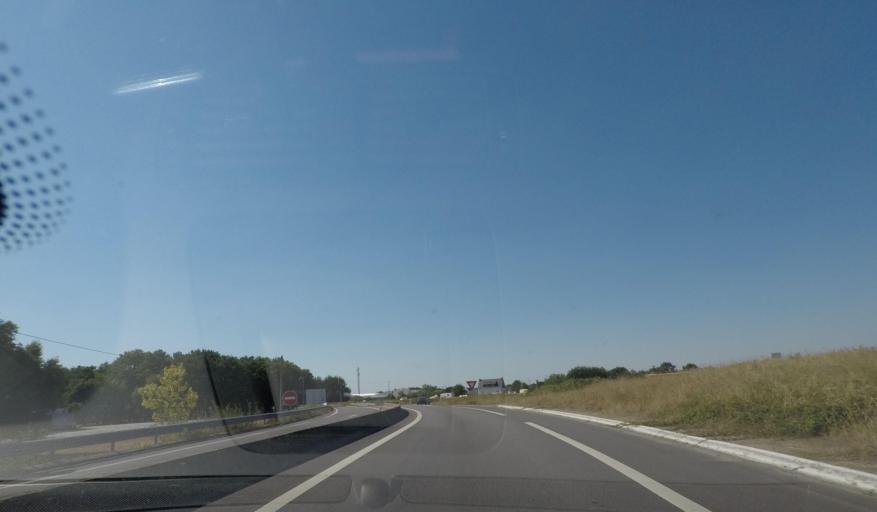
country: FR
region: Brittany
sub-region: Departement du Morbihan
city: Peaule
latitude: 47.5354
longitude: -2.3969
